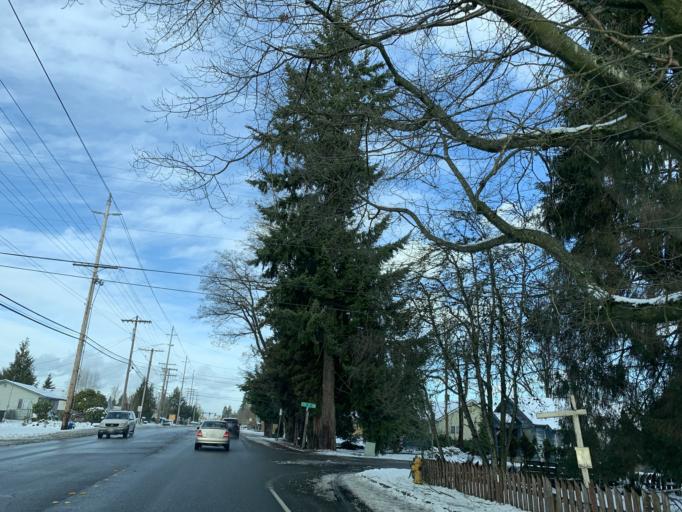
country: US
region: Washington
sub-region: Snohomish County
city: Martha Lake
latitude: 47.9025
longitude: -122.2389
